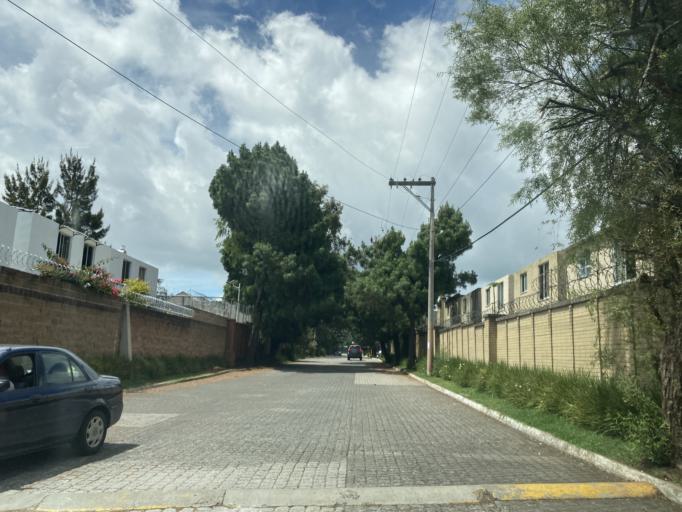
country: GT
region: Guatemala
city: San Jose Pinula
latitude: 14.5400
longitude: -90.4354
